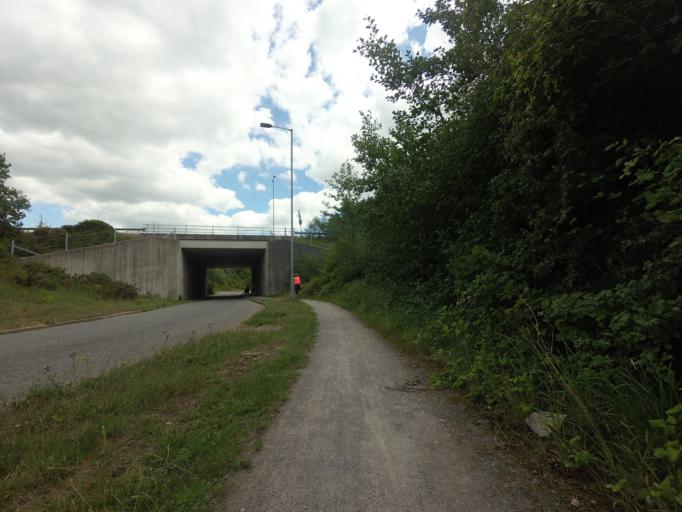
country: GB
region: England
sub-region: East Sussex
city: Hailsham
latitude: 50.8299
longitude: 0.2383
